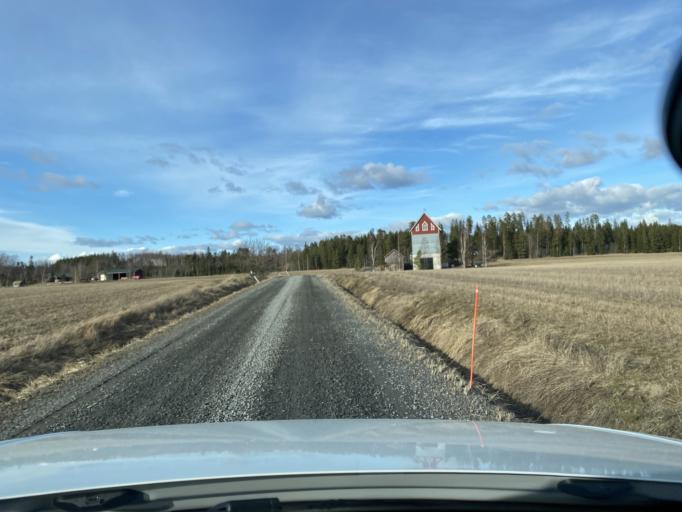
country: FI
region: Pirkanmaa
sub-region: Lounais-Pirkanmaa
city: Punkalaidun
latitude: 61.1350
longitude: 23.2079
